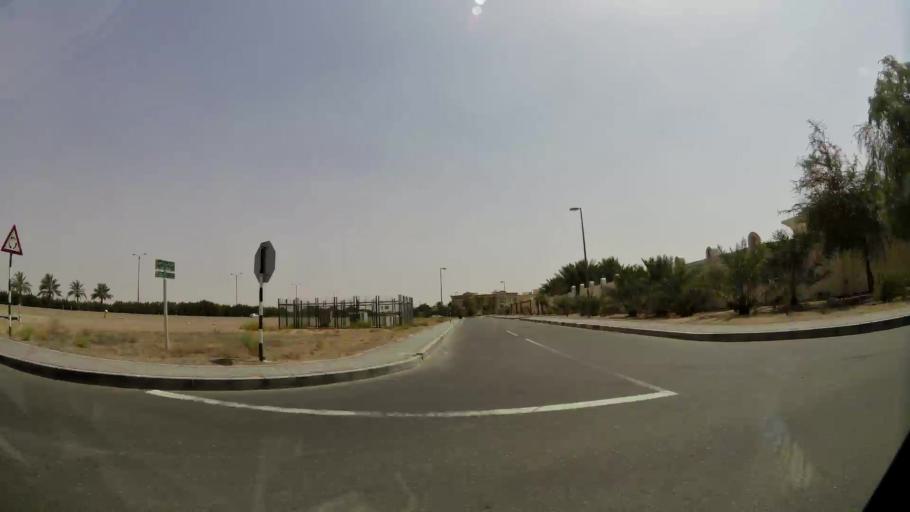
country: AE
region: Abu Dhabi
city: Al Ain
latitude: 24.1514
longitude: 55.6562
